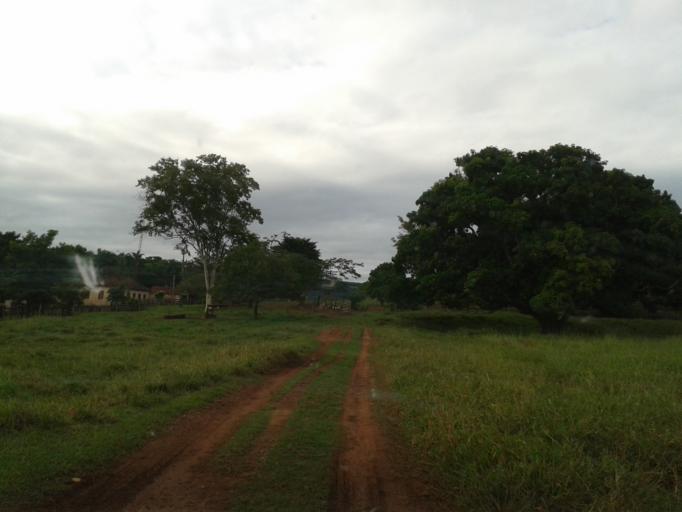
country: BR
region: Minas Gerais
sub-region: Campina Verde
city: Campina Verde
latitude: -19.4712
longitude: -49.6357
